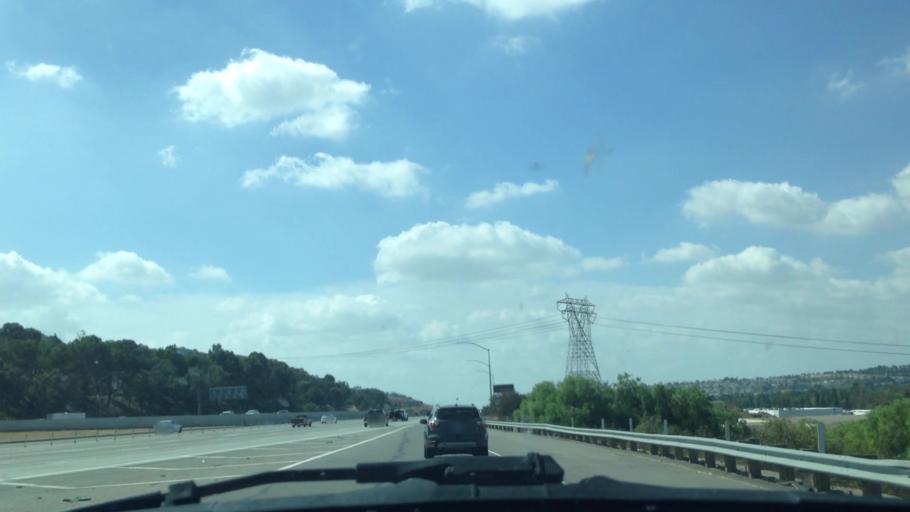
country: US
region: California
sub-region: Orange County
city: Yorba Linda
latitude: 33.8705
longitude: -117.7476
